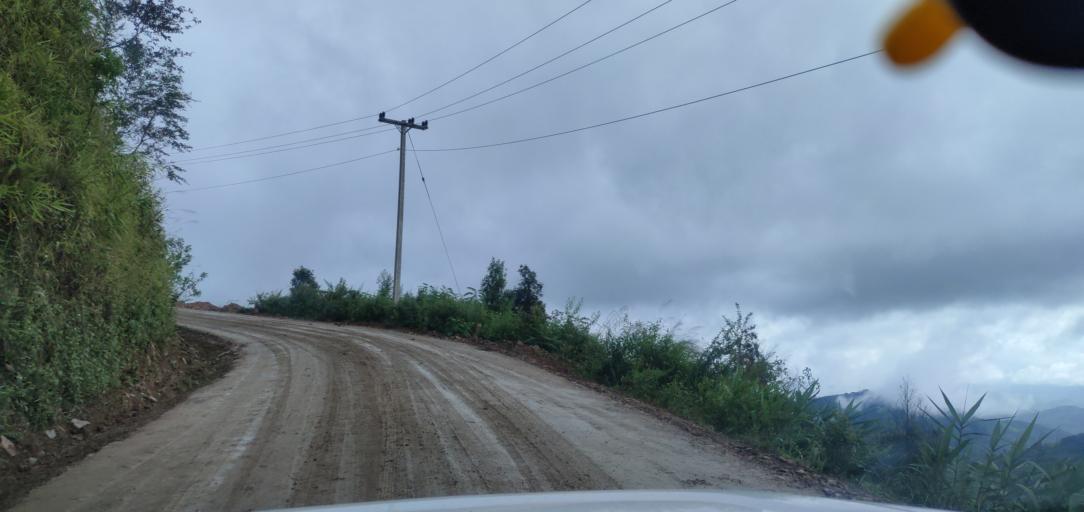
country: LA
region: Phongsali
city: Phongsali
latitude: 21.4232
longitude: 102.1741
